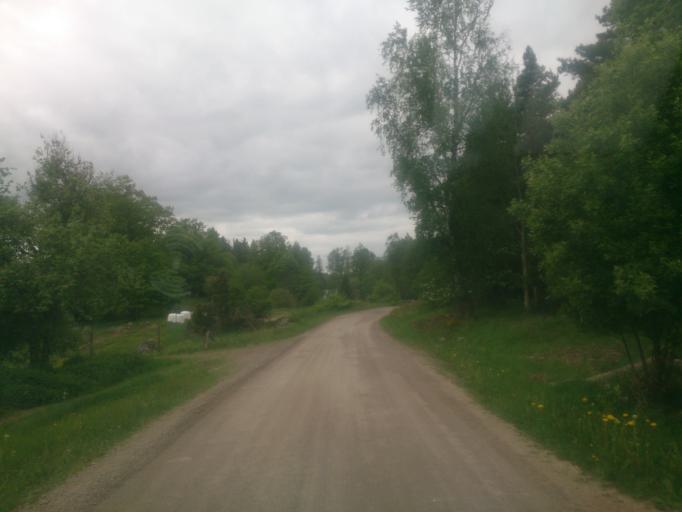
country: SE
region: OEstergoetland
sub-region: Atvidabergs Kommun
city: Atvidaberg
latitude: 58.2270
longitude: 16.0756
